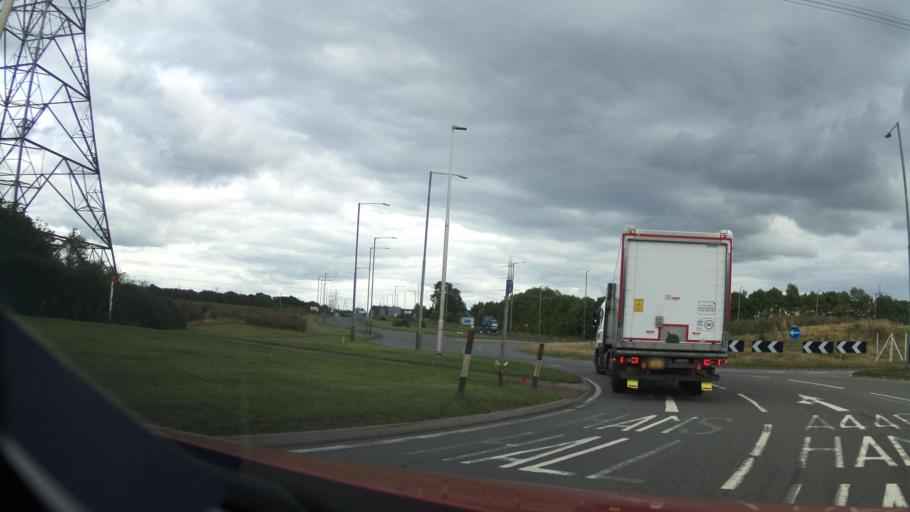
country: GB
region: England
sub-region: Warwickshire
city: Curdworth
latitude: 52.5303
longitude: -1.7231
